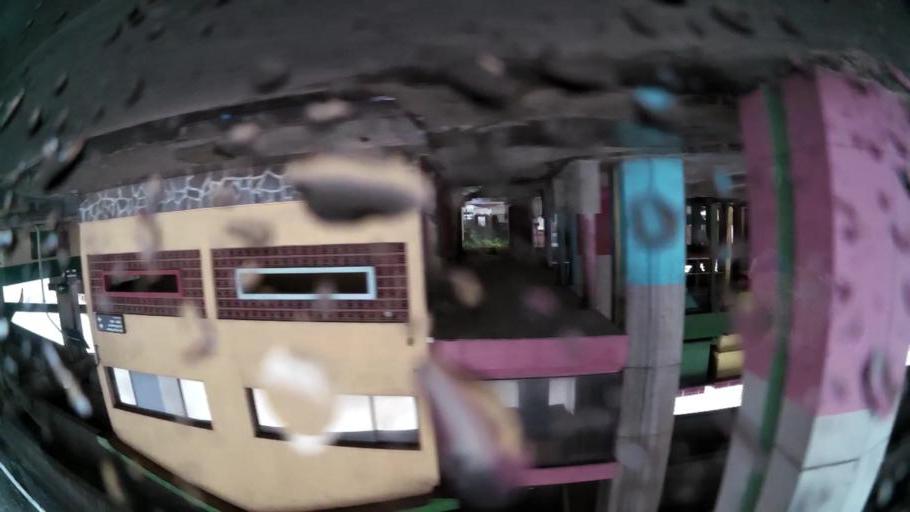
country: AR
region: Buenos Aires F.D.
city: Buenos Aires
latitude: -34.6314
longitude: -58.3538
